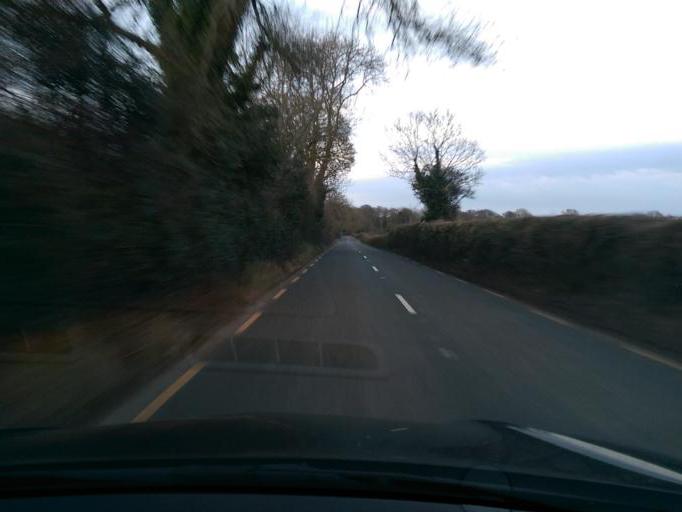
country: IE
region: Leinster
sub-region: Uibh Fhaili
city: Banagher
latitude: 53.0826
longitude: -8.0636
